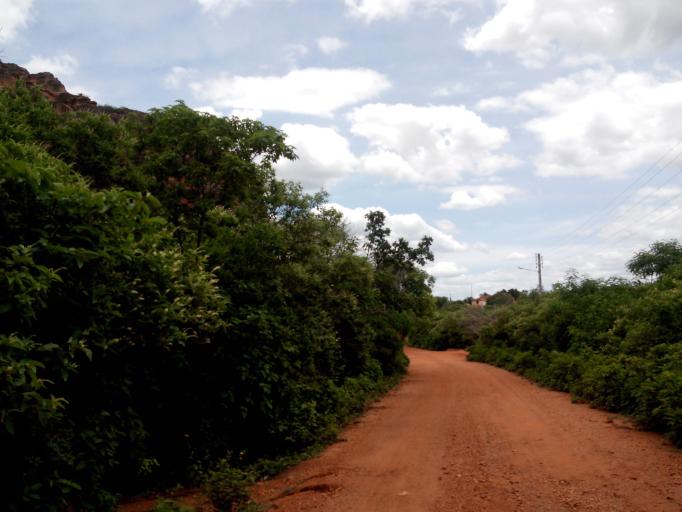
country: BR
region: Piaui
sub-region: Sao Raimundo Nonato
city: Sao Raimundo Nonato
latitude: -8.8440
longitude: -42.5585
